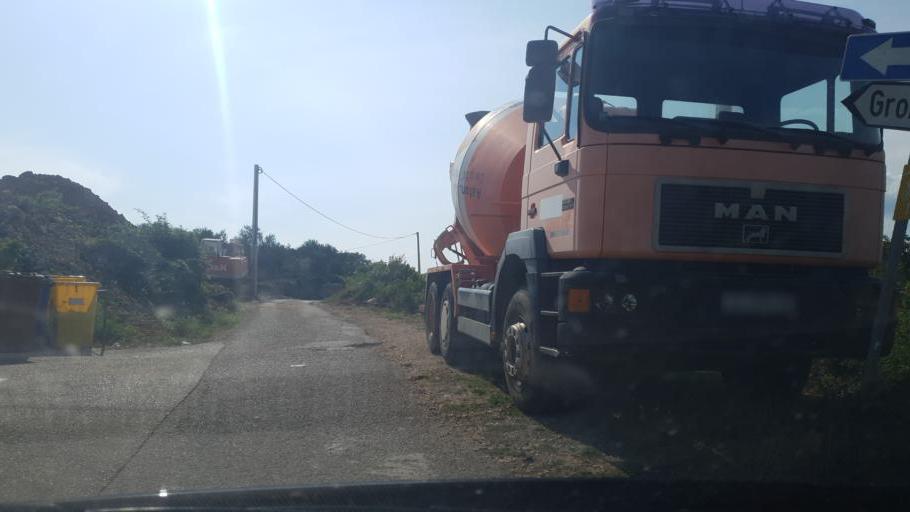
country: HR
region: Primorsko-Goranska
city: Punat
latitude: 45.0760
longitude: 14.6679
